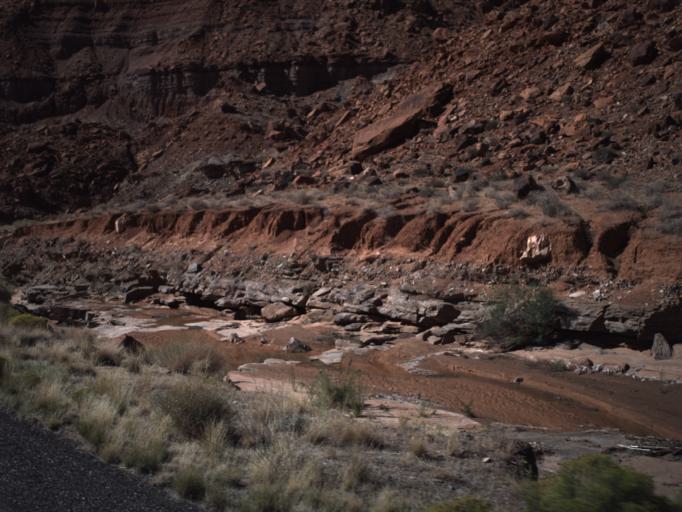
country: US
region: Utah
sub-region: San Juan County
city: Blanding
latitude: 37.9269
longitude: -110.4646
